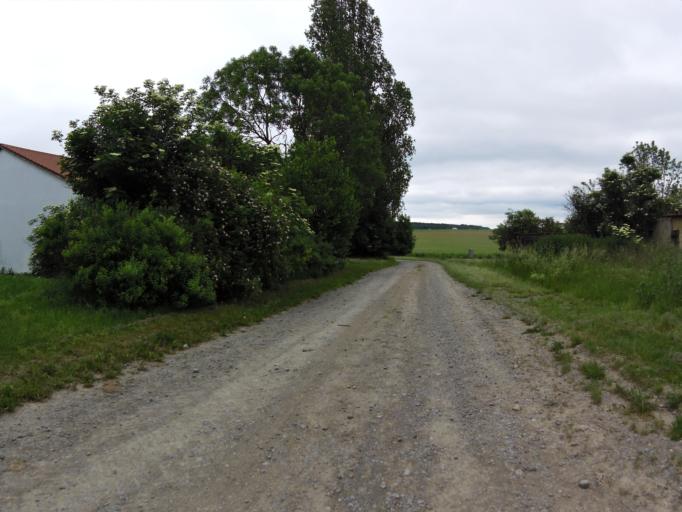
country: DE
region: Bavaria
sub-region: Regierungsbezirk Unterfranken
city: Waldbuttelbrunn
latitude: 49.8040
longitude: 9.8483
